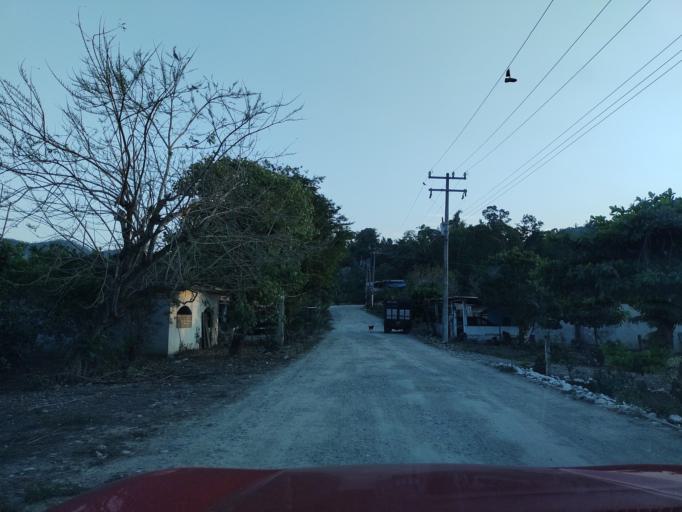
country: MX
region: Veracruz
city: Agua Dulce
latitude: 20.3138
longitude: -97.2750
